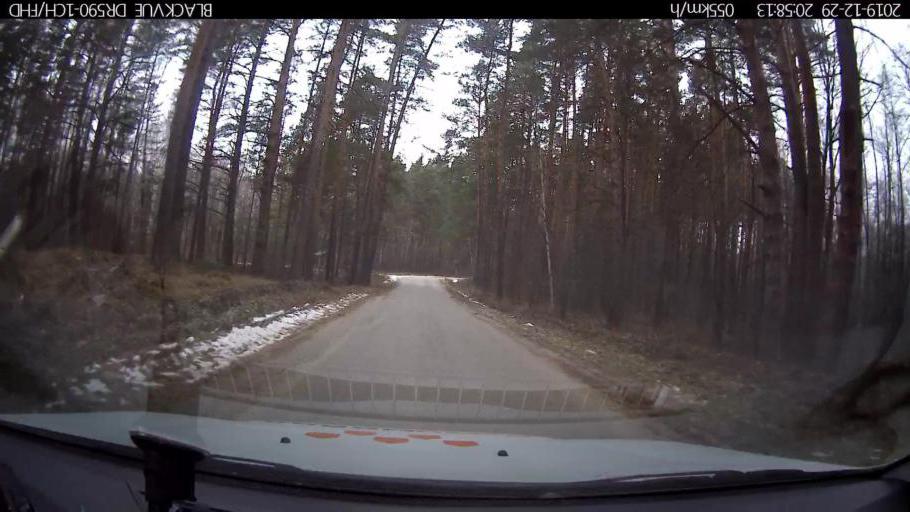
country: RU
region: Nizjnij Novgorod
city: Afonino
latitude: 56.1671
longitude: 43.9876
